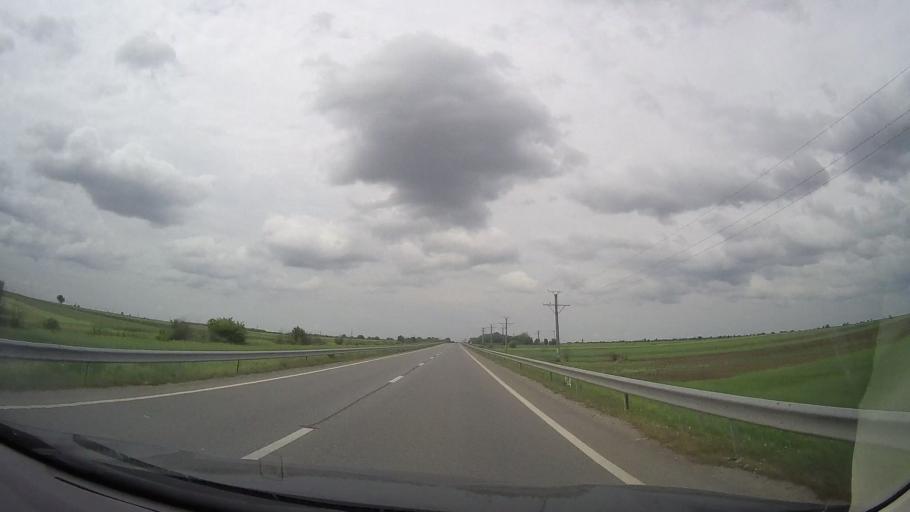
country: RO
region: Dolj
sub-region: Comuna Leu
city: Leu
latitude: 44.1798
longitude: 24.0314
